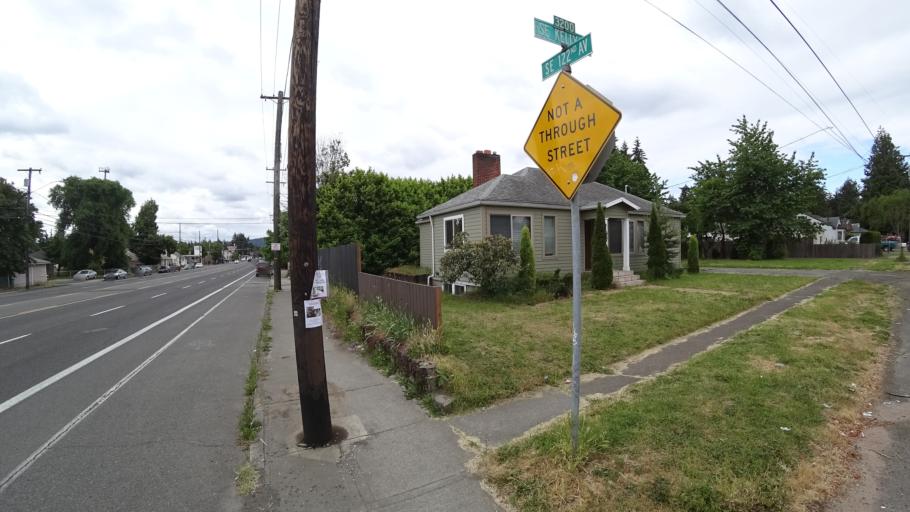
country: US
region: Oregon
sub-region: Multnomah County
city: Lents
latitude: 45.4991
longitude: -122.5378
